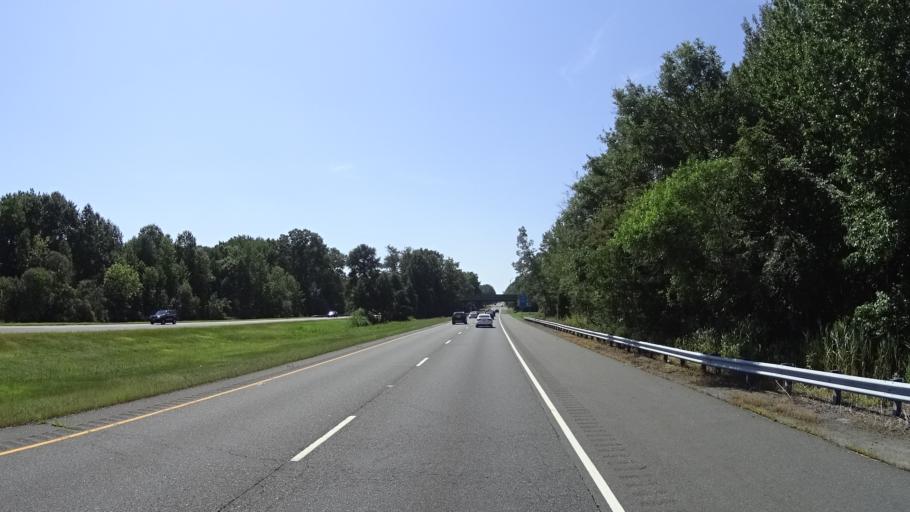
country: US
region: New Jersey
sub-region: Monmouth County
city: Wanamassa
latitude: 40.2548
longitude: -74.0570
